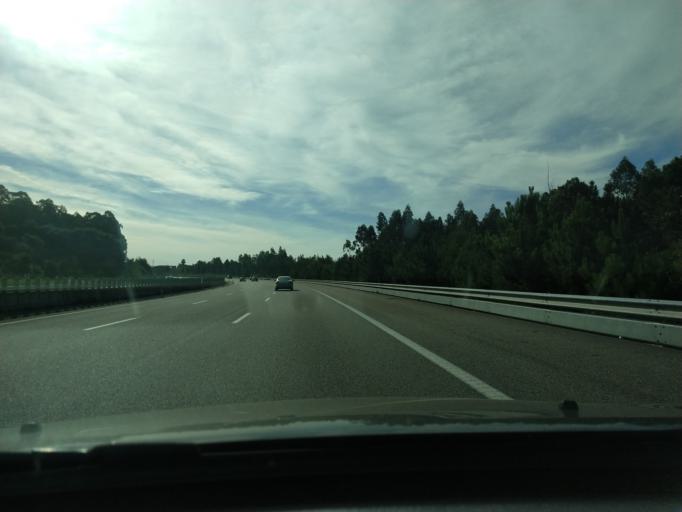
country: PT
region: Aveiro
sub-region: Ovar
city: Sao Joao
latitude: 40.8889
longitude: -8.5679
